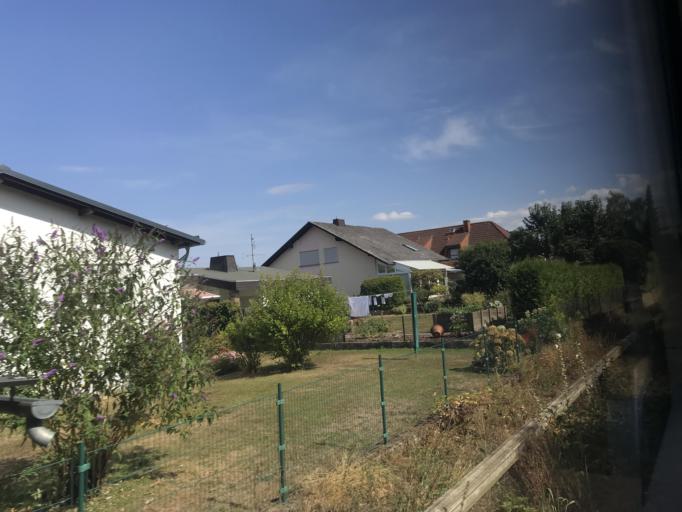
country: DE
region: Hesse
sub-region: Regierungsbezirk Giessen
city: Elz
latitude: 50.4121
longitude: 8.0223
